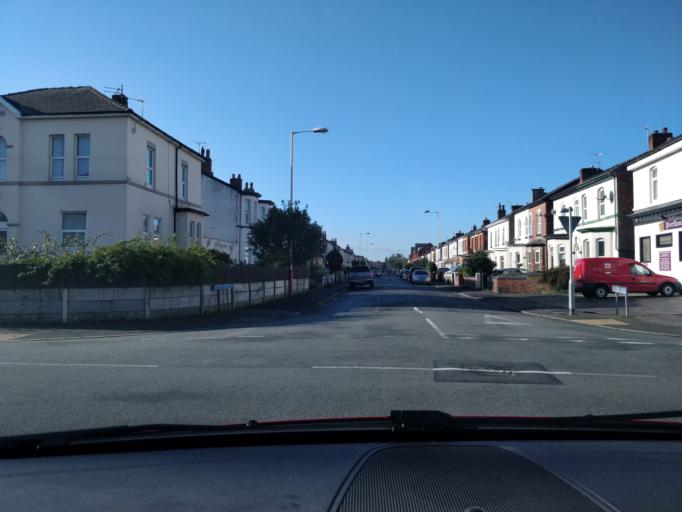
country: GB
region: England
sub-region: Sefton
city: Southport
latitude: 53.6390
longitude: -2.9997
